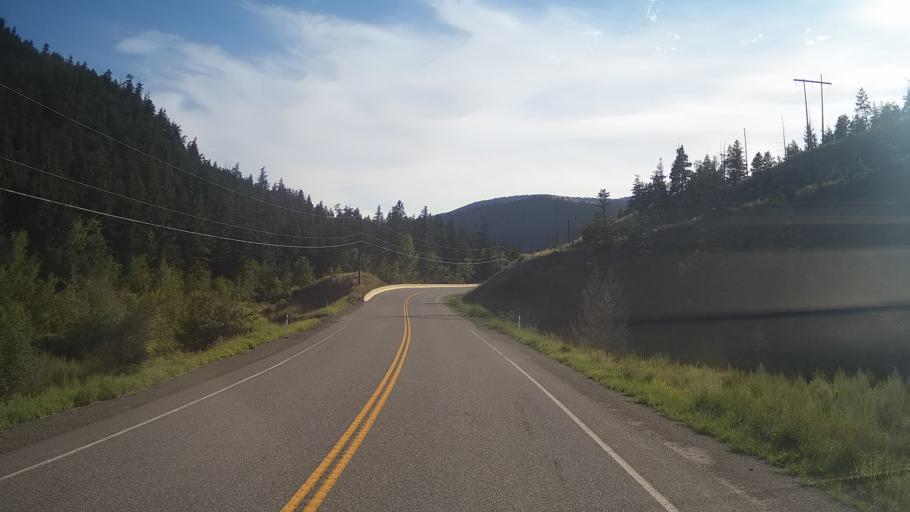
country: CA
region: British Columbia
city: Cache Creek
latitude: 50.8841
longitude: -121.4967
